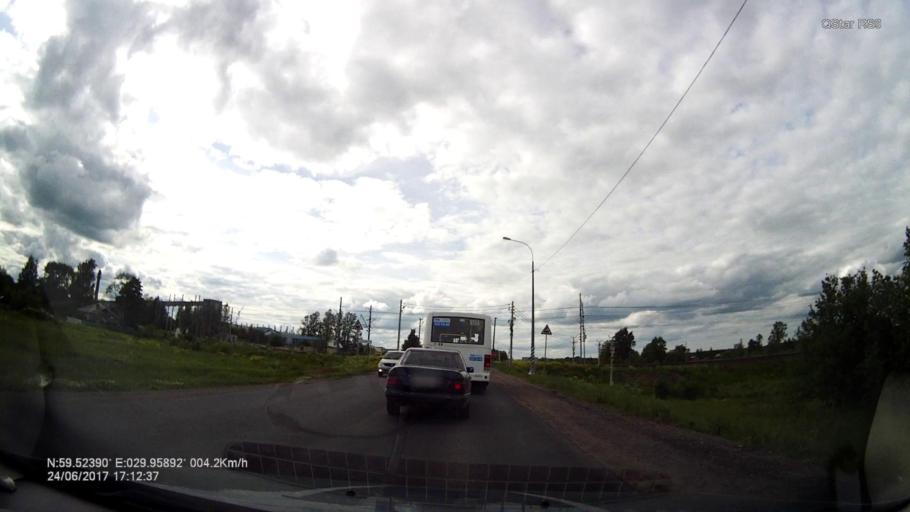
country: RU
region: Leningrad
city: Voyskovitsy
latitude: 59.5239
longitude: 29.9589
